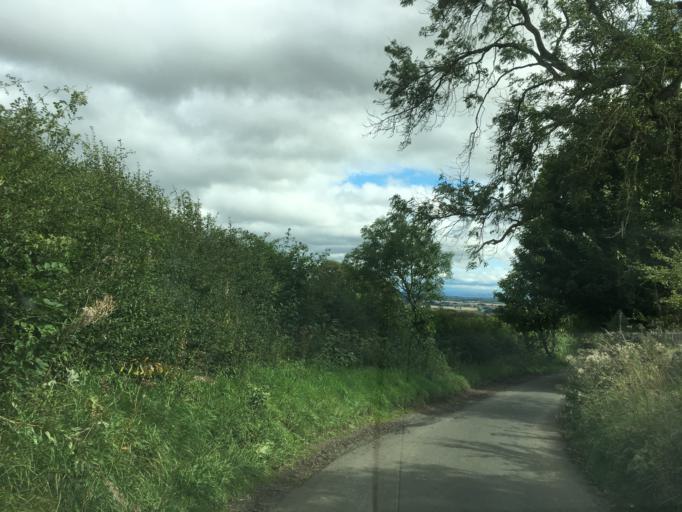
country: GB
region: Scotland
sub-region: West Lothian
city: Linlithgow
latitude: 55.9970
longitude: -3.5951
